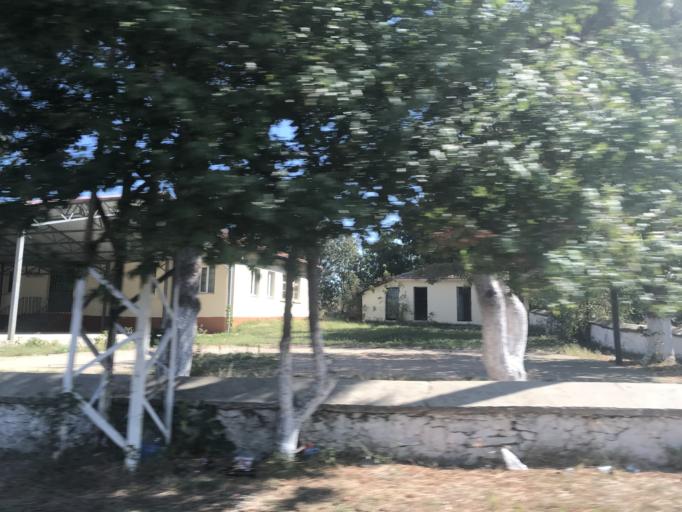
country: TR
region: Kirklareli
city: Kirklareli
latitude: 41.7751
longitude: 27.2267
